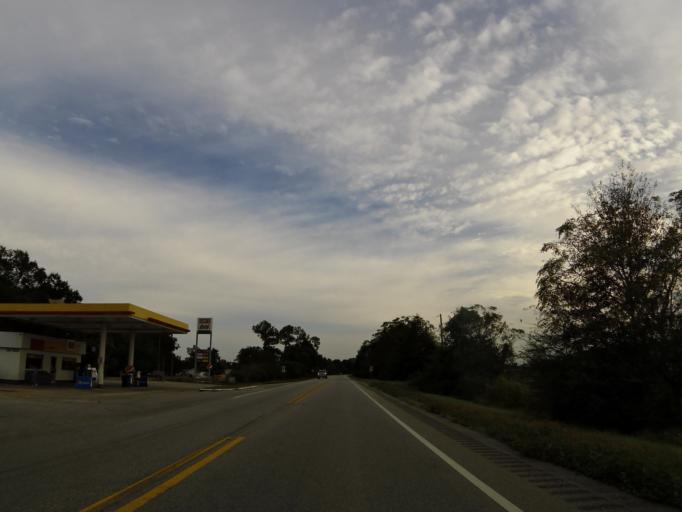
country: US
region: Alabama
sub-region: Monroe County
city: Frisco City
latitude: 31.3802
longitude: -87.4287
